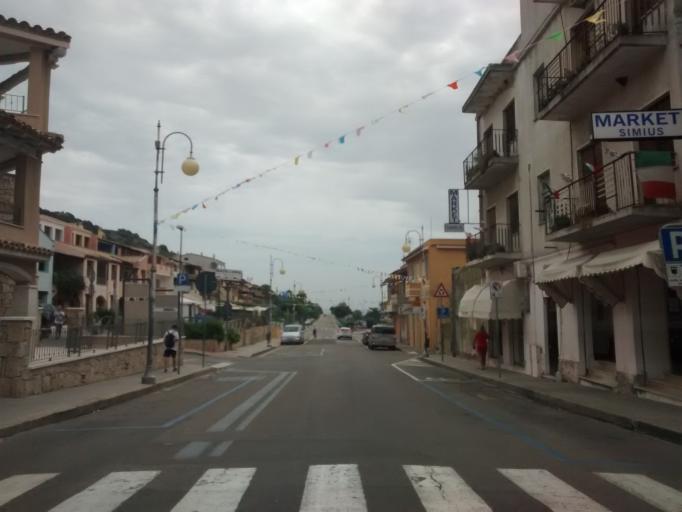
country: IT
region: Sardinia
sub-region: Provincia di Cagliari
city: Villasimius
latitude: 39.1397
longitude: 9.5221
